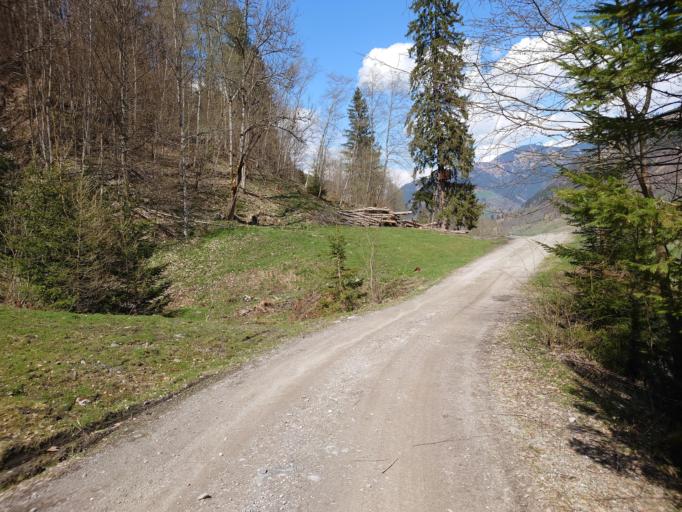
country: AT
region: Salzburg
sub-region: Politischer Bezirk Zell am See
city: Bruck an der Grossglocknerstrasse
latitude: 47.2406
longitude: 12.8190
